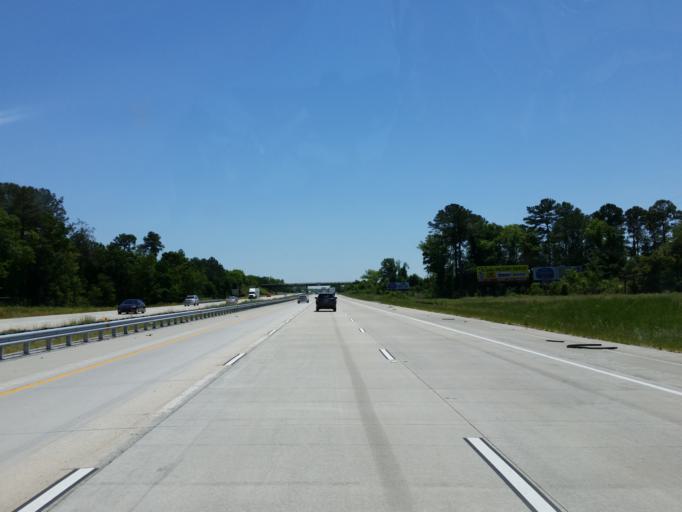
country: US
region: Georgia
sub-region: Dooly County
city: Vienna
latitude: 32.0640
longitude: -83.7636
